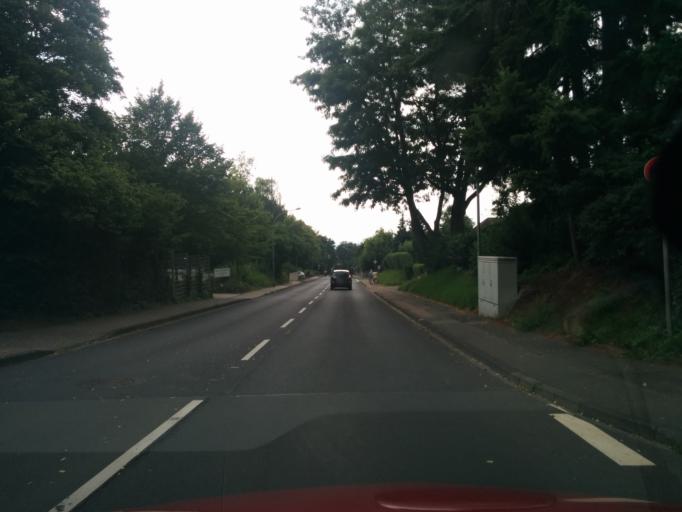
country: DE
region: Rheinland-Pfalz
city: Koblenz
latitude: 50.3466
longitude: 7.6176
